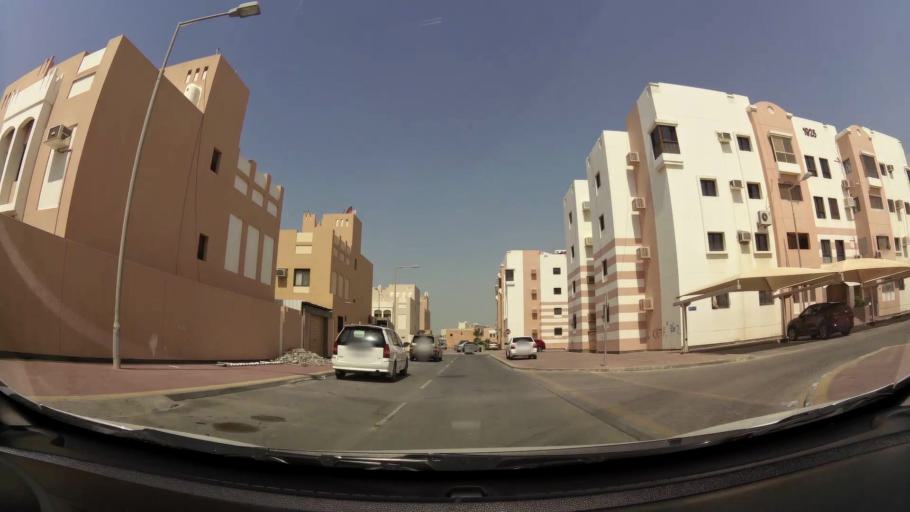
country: BH
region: Manama
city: Jidd Hafs
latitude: 26.2154
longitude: 50.4457
